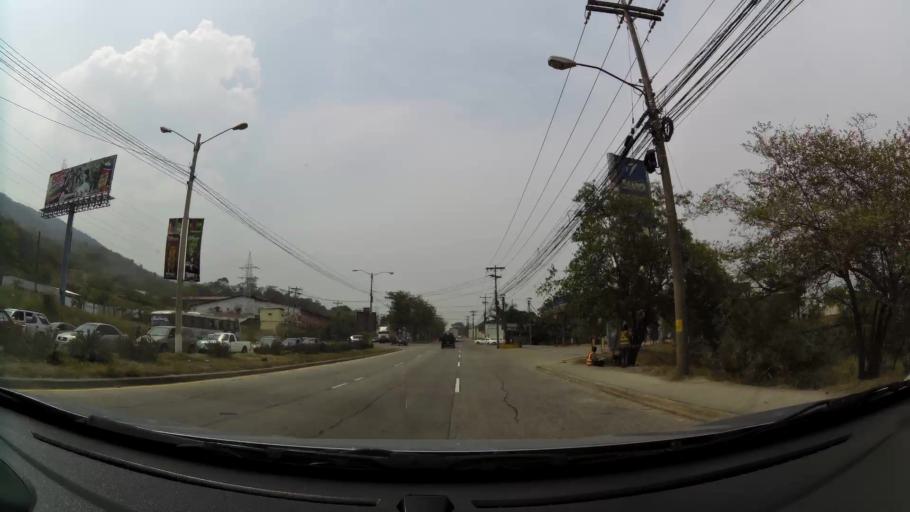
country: HN
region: Cortes
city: Chotepe
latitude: 15.4383
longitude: -88.0208
